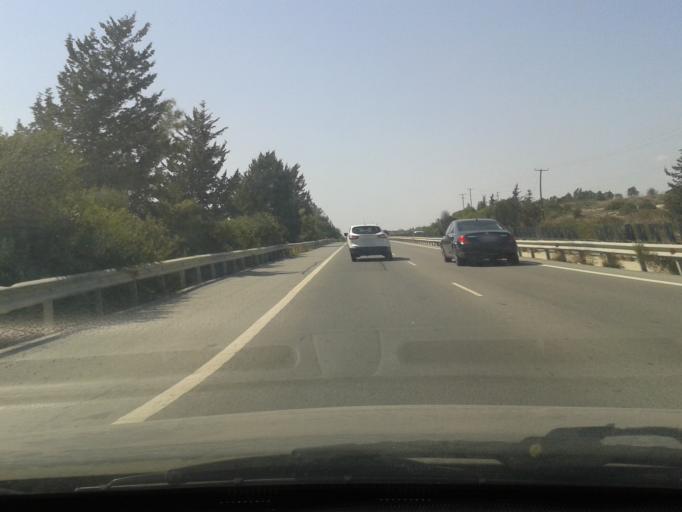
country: CY
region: Larnaka
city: Agios Tychon
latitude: 34.7175
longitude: 33.1441
